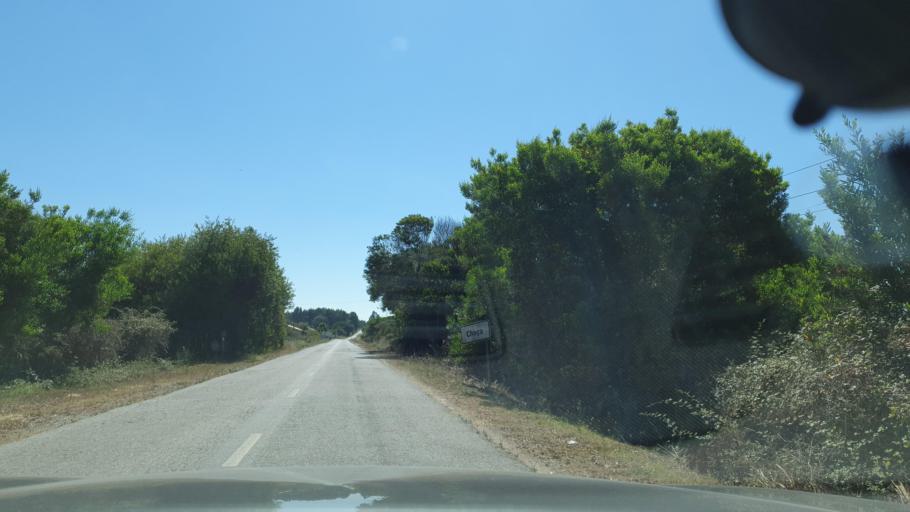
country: PT
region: Beja
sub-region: Odemira
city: Sao Teotonio
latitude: 37.5000
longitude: -8.6772
